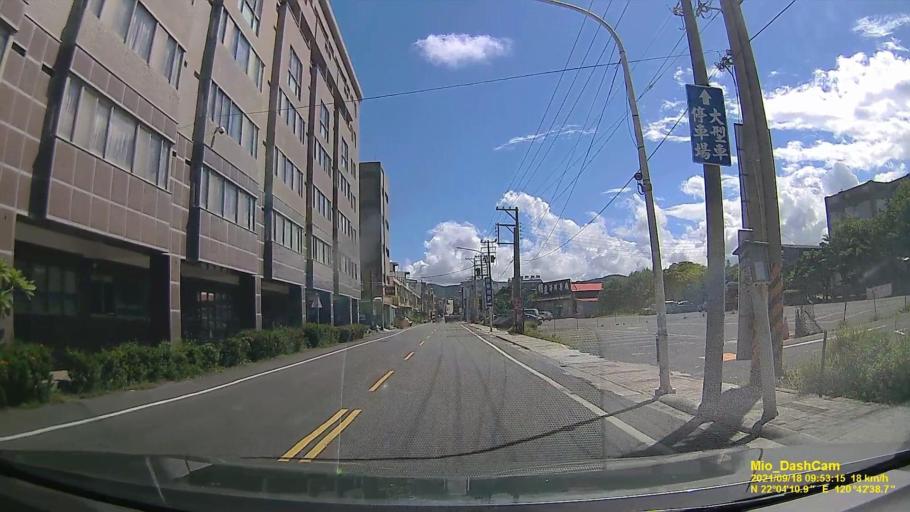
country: TW
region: Taiwan
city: Hengchun
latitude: 22.0697
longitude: 120.7107
